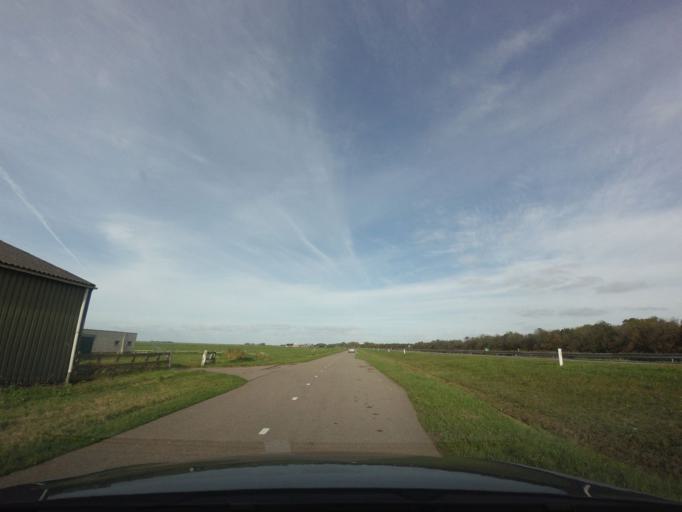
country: NL
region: North Holland
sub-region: Gemeente Schagen
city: Harenkarspel
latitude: 52.7151
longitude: 4.7089
